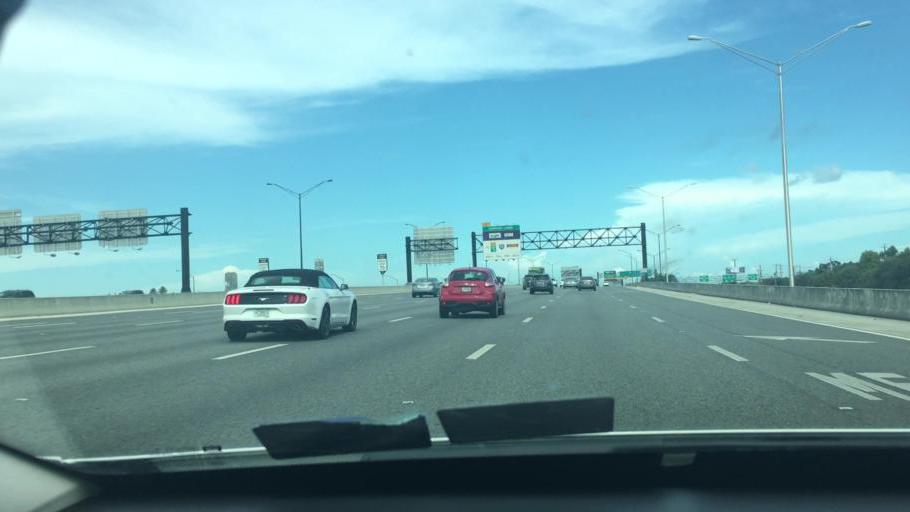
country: US
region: Florida
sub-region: Broward County
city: Southwest Ranches
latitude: 26.1180
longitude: -80.3346
